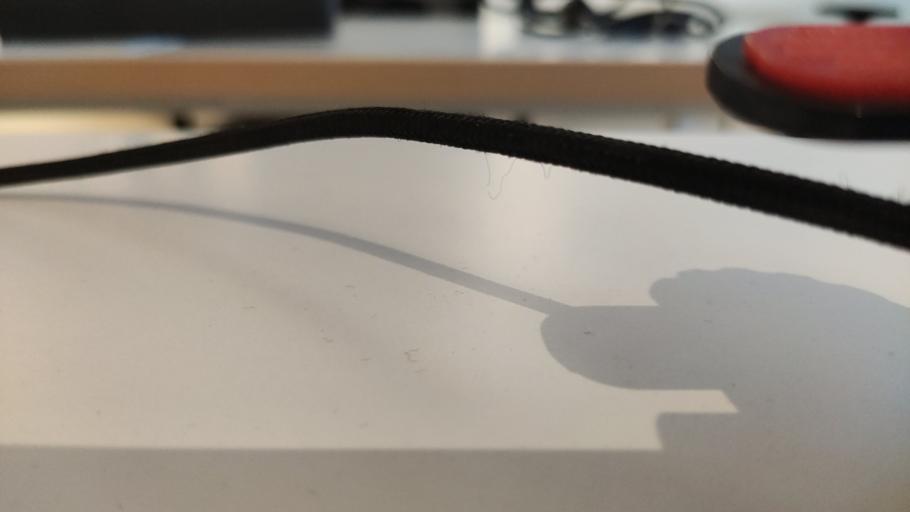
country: RU
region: Moskovskaya
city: Ruza
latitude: 55.8150
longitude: 36.2981
